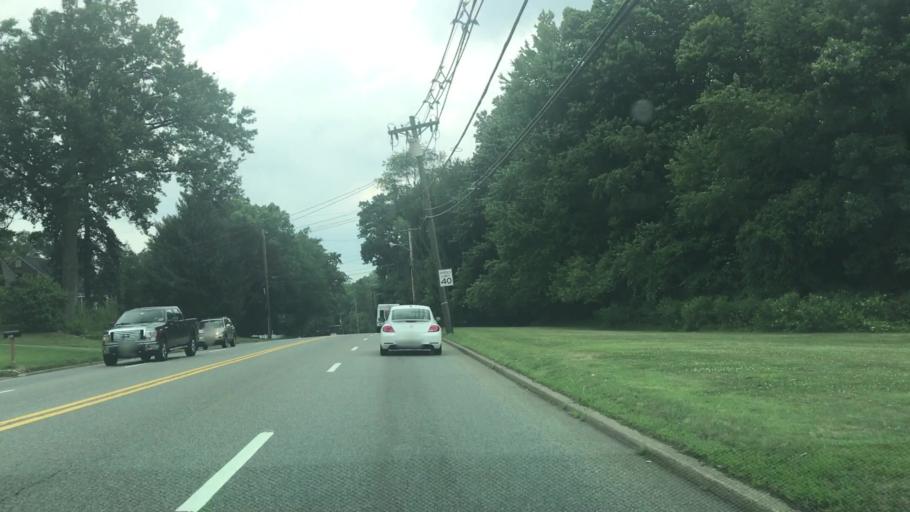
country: US
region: New Jersey
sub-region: Bergen County
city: River Edge
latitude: 40.9235
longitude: -74.0519
